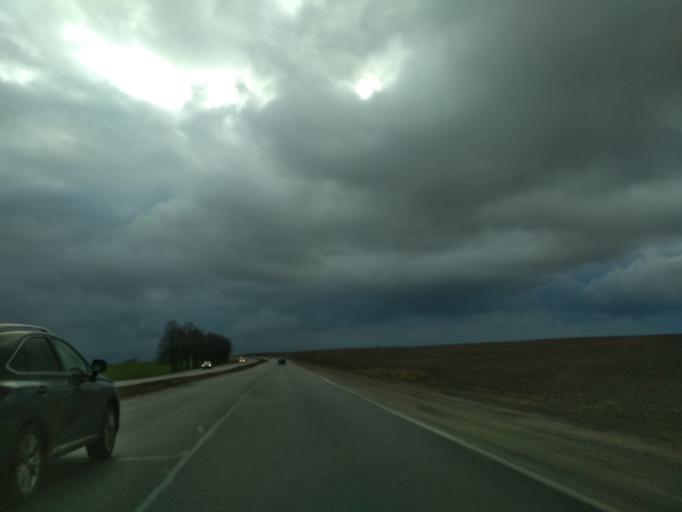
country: BY
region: Minsk
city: Luhavaya Slabada
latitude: 53.7555
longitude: 27.8311
